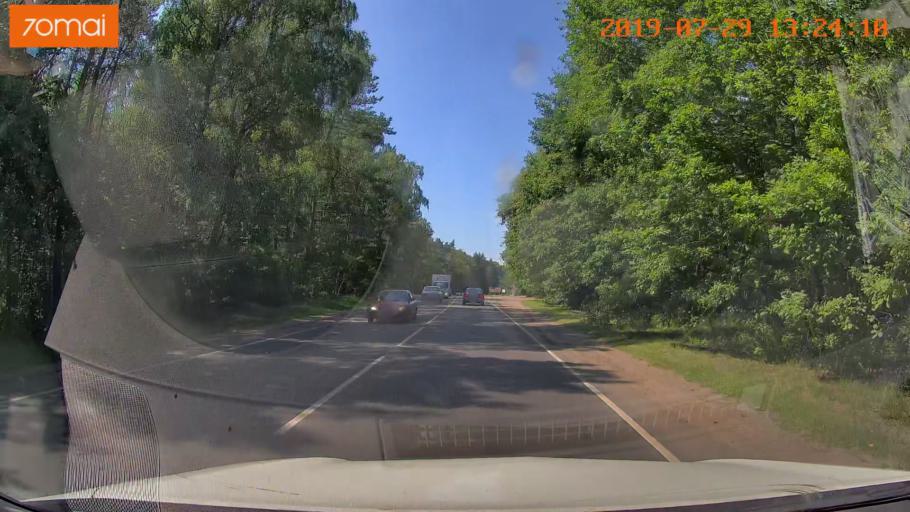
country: RU
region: Kaliningrad
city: Vzmorye
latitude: 54.7137
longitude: 20.3524
